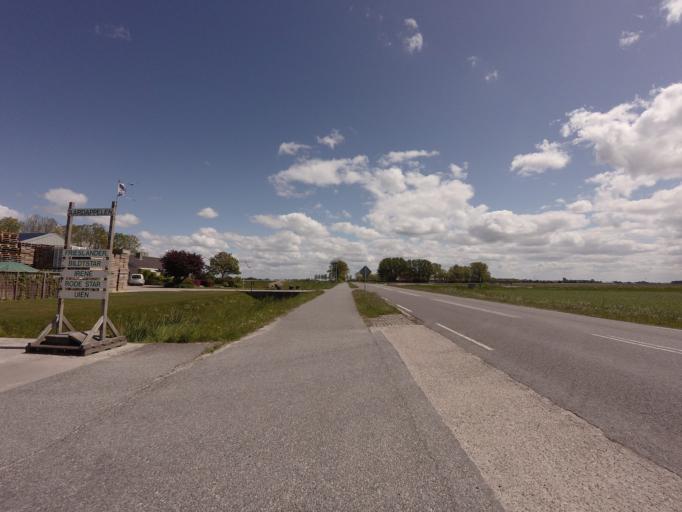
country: NL
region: Friesland
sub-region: Gemeente Harlingen
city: Harlingen
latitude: 53.1364
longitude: 5.4602
